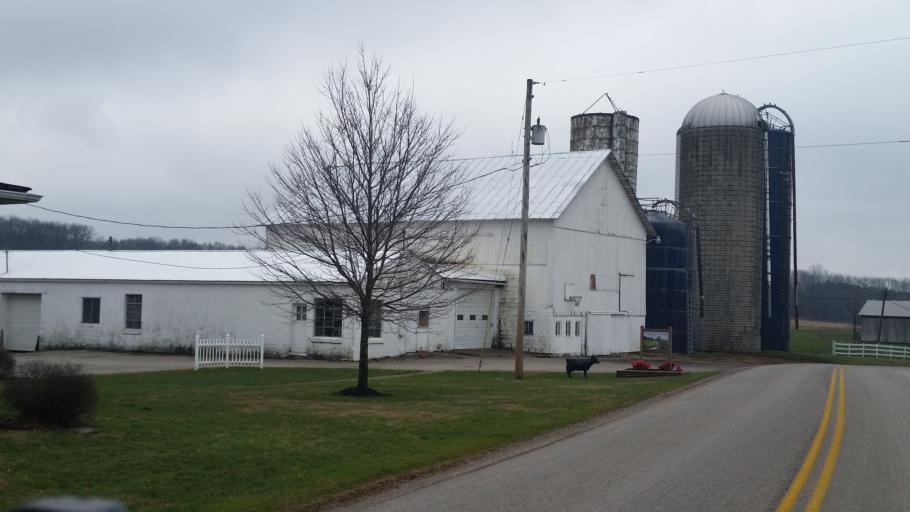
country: US
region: Ohio
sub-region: Richland County
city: Lexington
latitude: 40.6244
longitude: -82.6228
